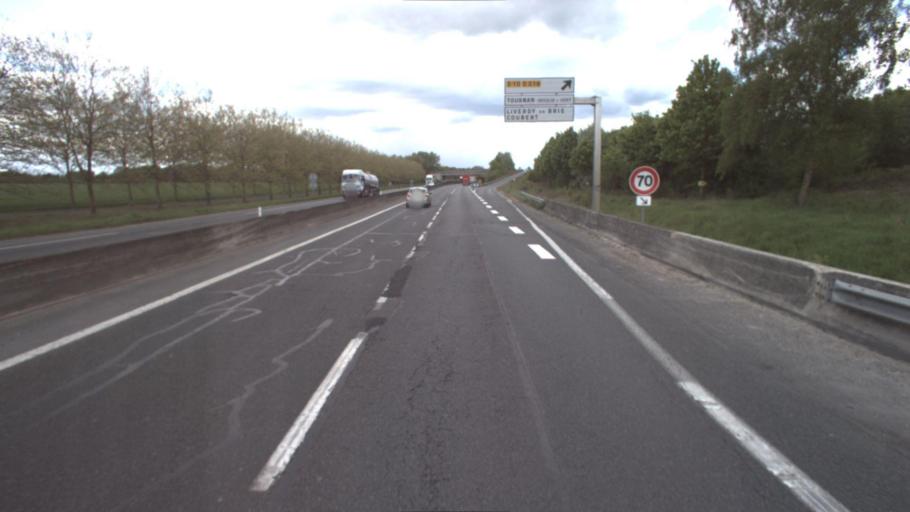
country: FR
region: Ile-de-France
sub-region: Departement de Seine-et-Marne
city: Tournan-en-Brie
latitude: 48.7334
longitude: 2.7825
